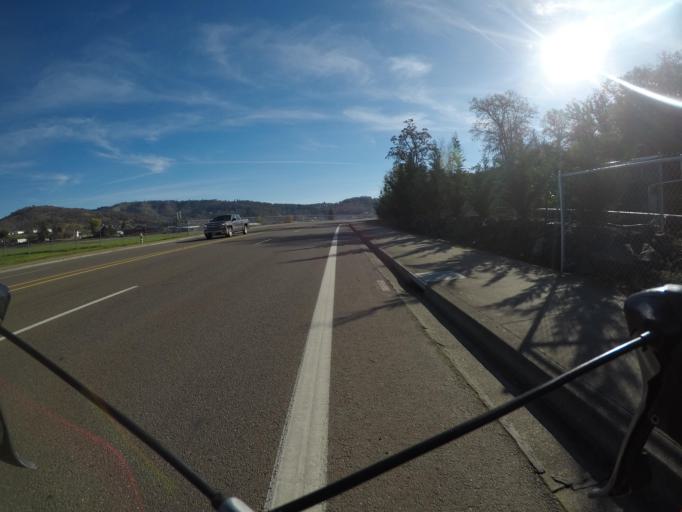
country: US
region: Oregon
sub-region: Douglas County
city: Roseburg
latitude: 43.2328
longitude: -123.3583
